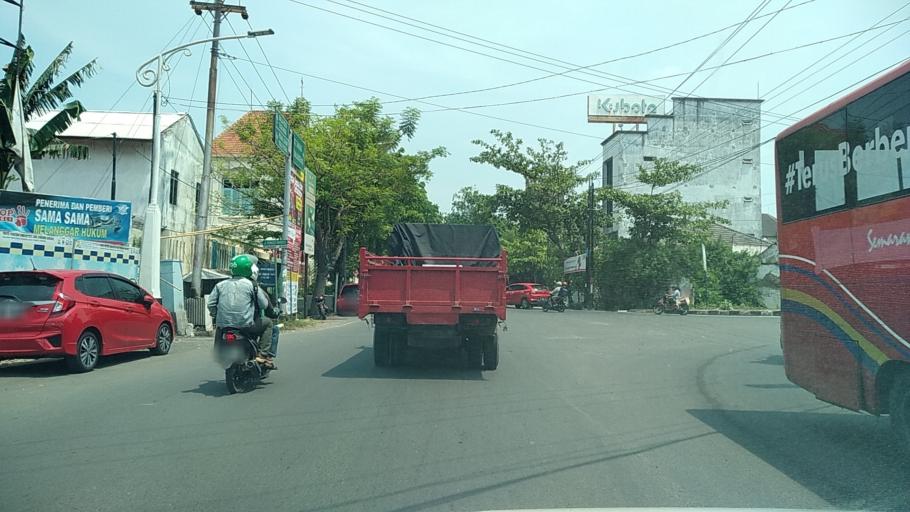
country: ID
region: Central Java
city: Semarang
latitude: -6.9673
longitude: 110.4310
